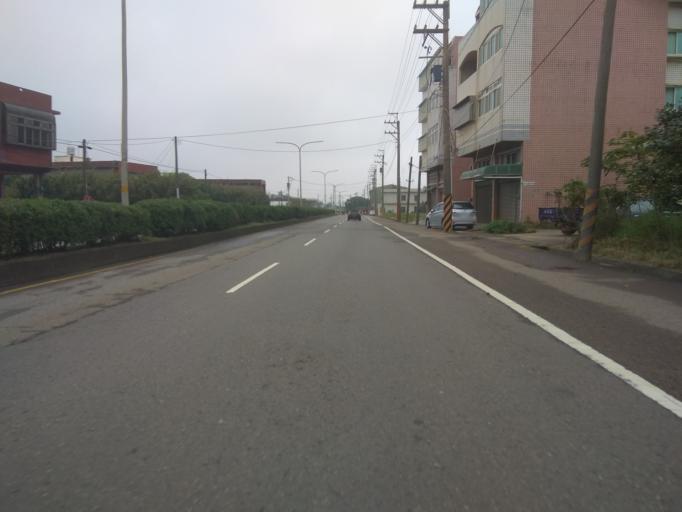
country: TW
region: Taiwan
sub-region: Hsinchu
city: Zhubei
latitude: 25.0004
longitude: 121.0368
